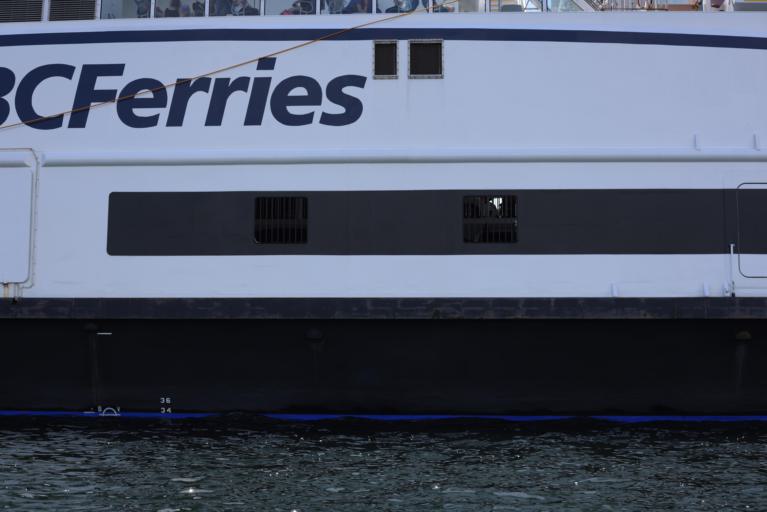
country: CA
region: British Columbia
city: Nanaimo
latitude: 49.1680
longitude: -123.9319
